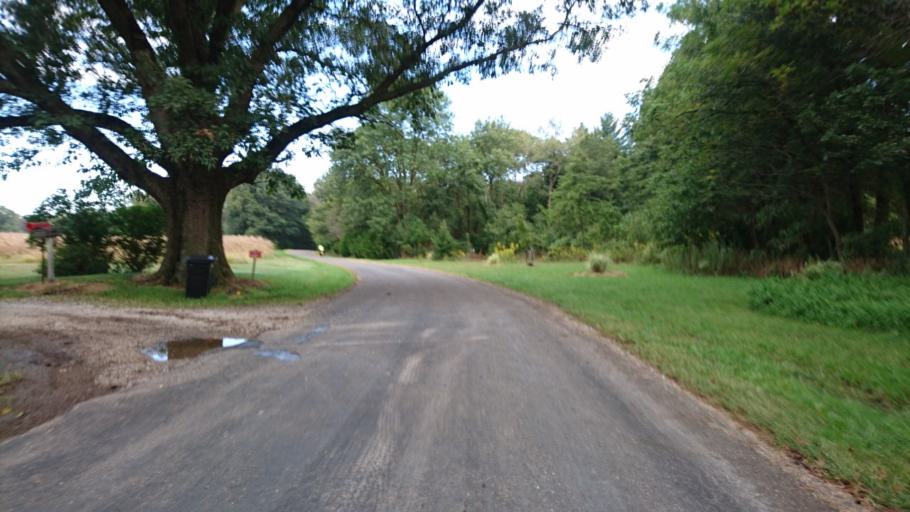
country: US
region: Illinois
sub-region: Macoupin County
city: Staunton
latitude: 38.9845
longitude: -89.7080
